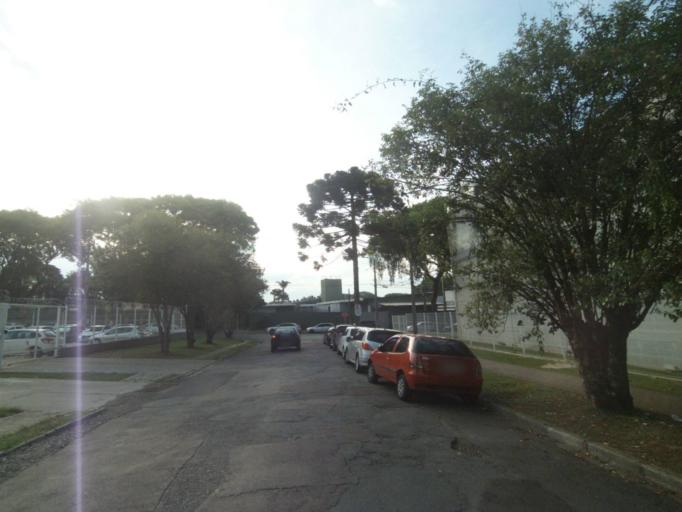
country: BR
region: Parana
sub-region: Pinhais
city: Pinhais
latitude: -25.4293
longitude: -49.2308
